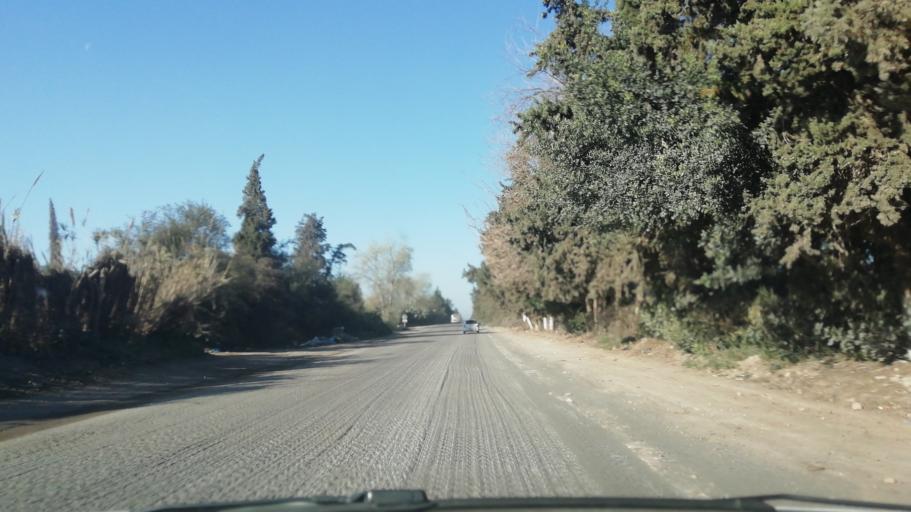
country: DZ
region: Mascara
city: Mascara
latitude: 35.5829
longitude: 0.0326
